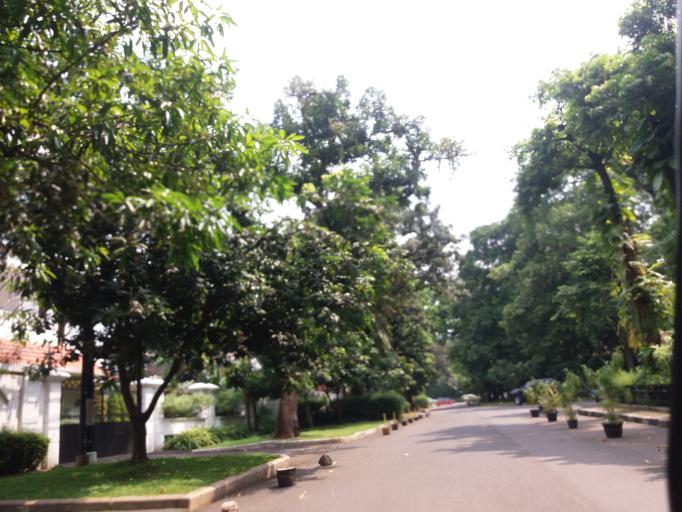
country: ID
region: Jakarta Raya
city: Jakarta
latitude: -6.2312
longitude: 106.8019
